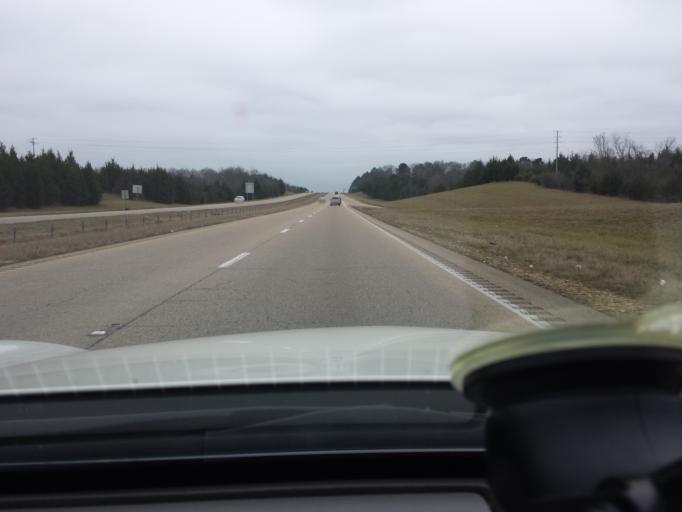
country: US
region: Mississippi
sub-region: Lee County
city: Verona
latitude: 34.2076
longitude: -88.7079
